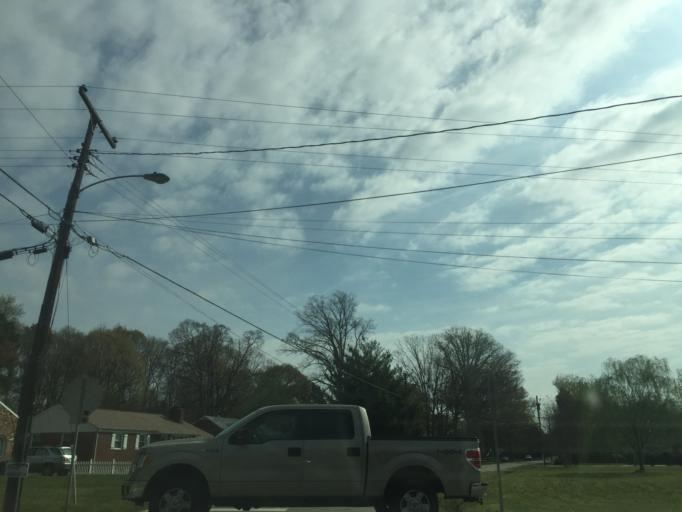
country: US
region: Virginia
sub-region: City of Newport News
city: Newport News
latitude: 37.0710
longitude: -76.4682
